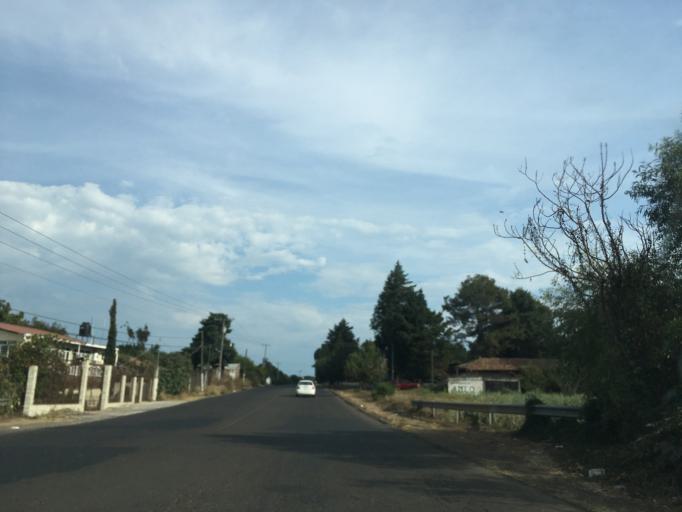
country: MX
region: Michoacan
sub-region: Tingueindin
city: Tingueindin
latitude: 19.7720
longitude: -102.4989
